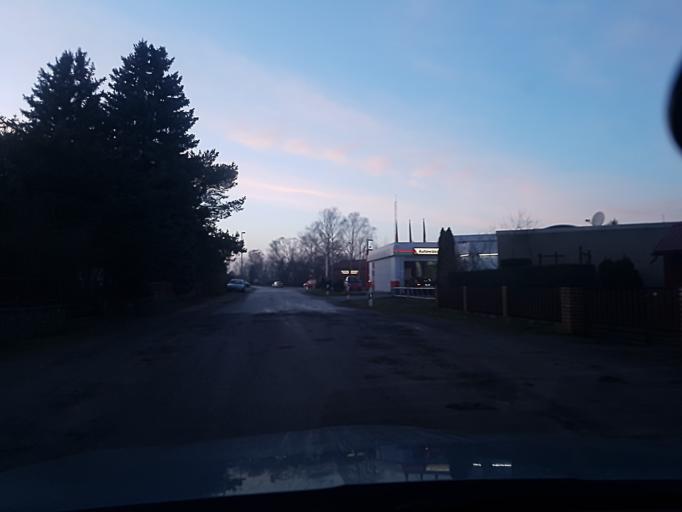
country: DE
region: Brandenburg
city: Doberlug-Kirchhain
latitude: 51.6263
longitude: 13.5825
